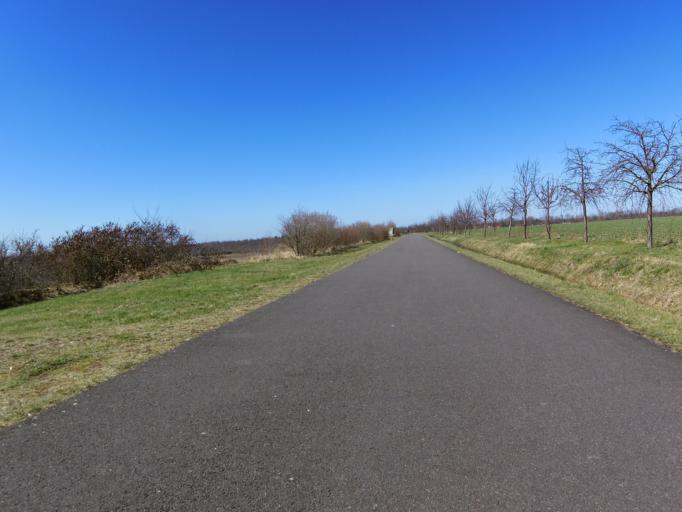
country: DE
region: Saxony
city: Markkleeberg
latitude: 51.2668
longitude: 12.4206
